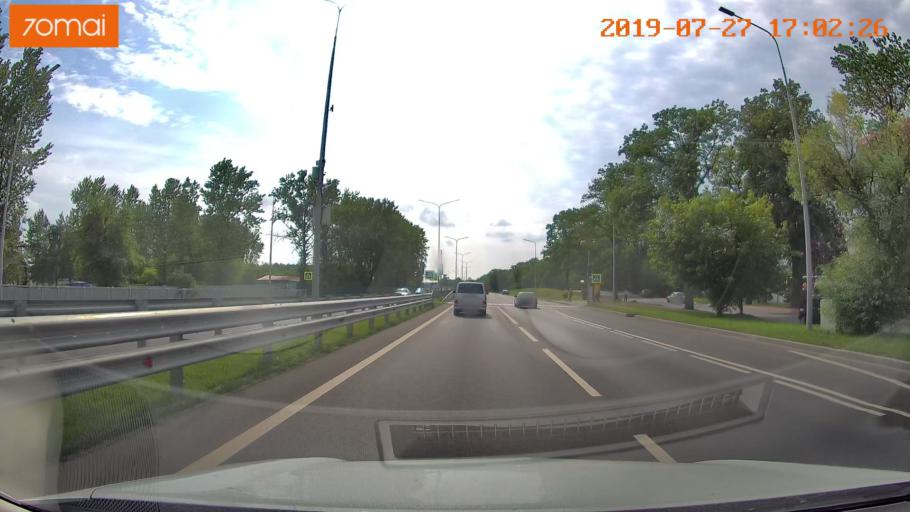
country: RU
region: Kaliningrad
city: Bol'shoe Isakovo
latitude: 54.7069
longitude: 20.6174
